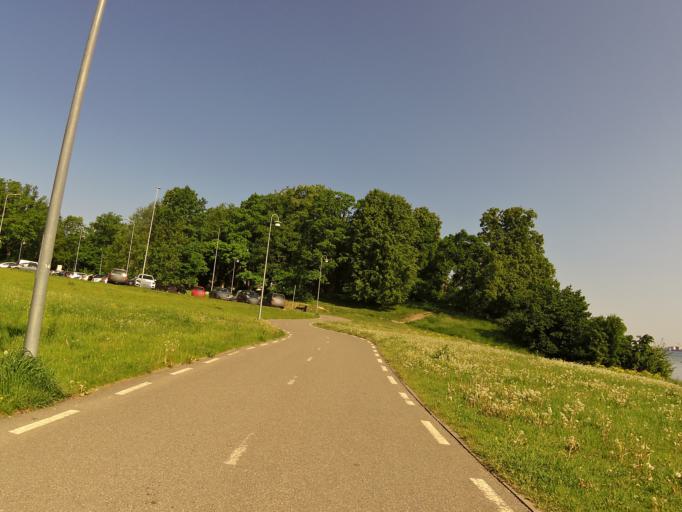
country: EE
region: Harju
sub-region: Saue vald
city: Laagri
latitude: 59.4301
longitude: 24.6527
